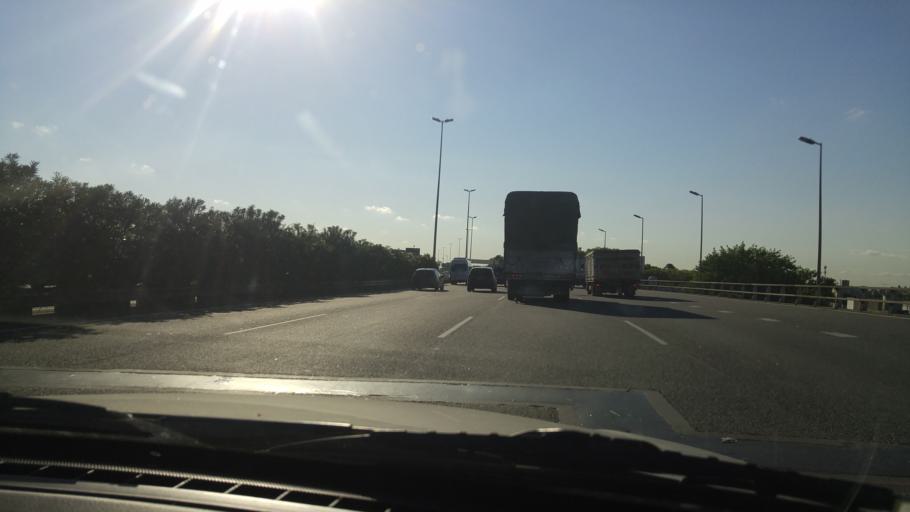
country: AR
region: Buenos Aires F.D.
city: Villa Santa Rita
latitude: -34.6448
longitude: -58.4874
